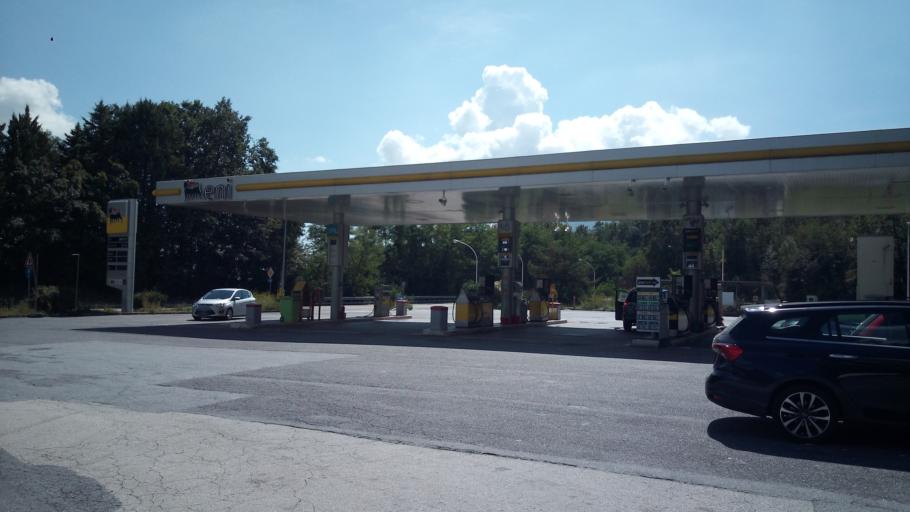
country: IT
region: Basilicate
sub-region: Provincia di Potenza
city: Rivello
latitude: 40.1033
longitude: 15.7437
